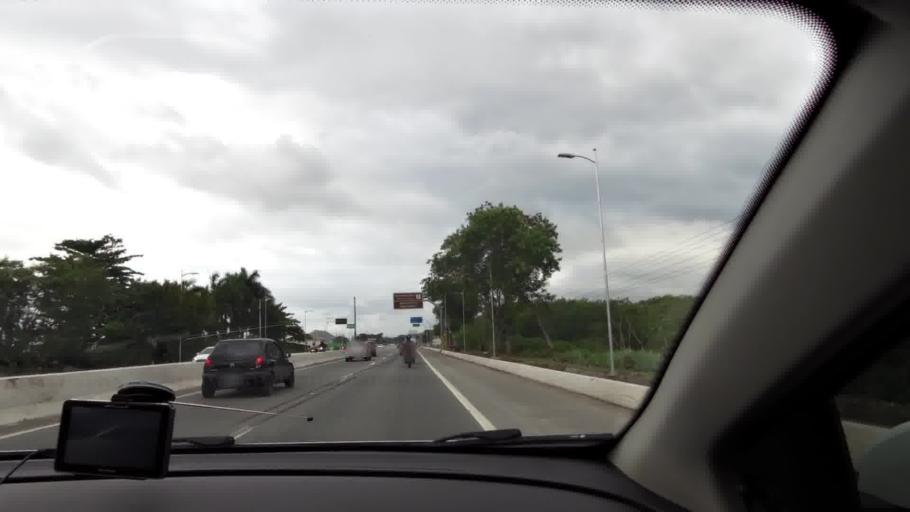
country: BR
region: Espirito Santo
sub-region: Vila Velha
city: Vila Velha
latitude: -20.2529
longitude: -40.2880
